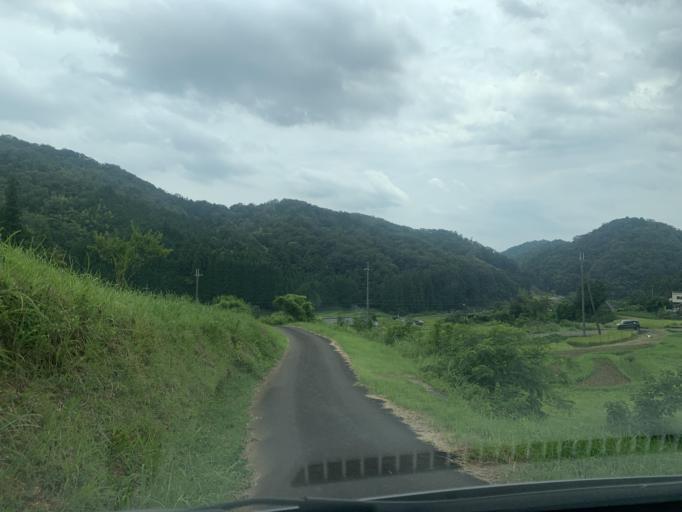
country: JP
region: Kyoto
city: Miyazu
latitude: 35.4479
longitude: 135.1621
